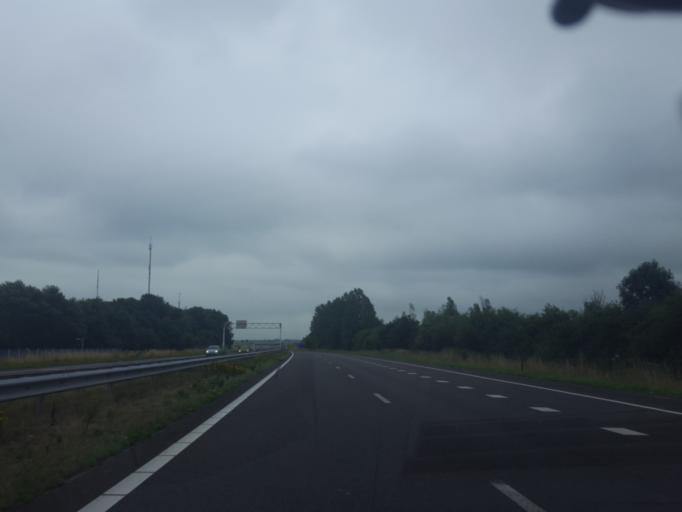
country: NL
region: Friesland
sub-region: Gemeente Boarnsterhim
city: Grou
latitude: 53.0863
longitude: 5.8251
